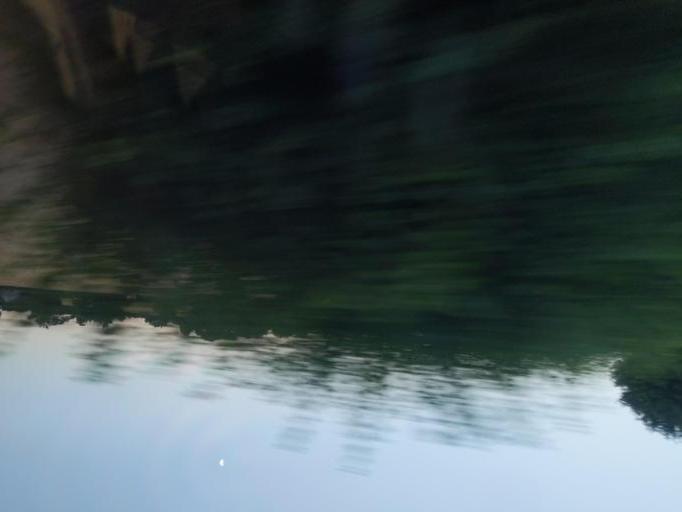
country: GB
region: England
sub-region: Devon
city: Ipplepen
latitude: 50.4696
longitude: -3.6618
